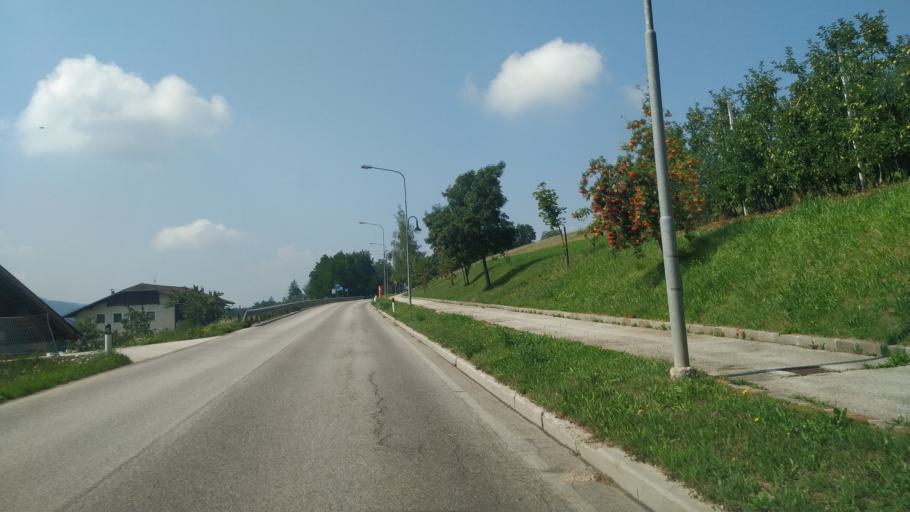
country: IT
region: Trentino-Alto Adige
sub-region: Provincia di Trento
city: Romeno
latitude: 46.4006
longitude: 11.1281
